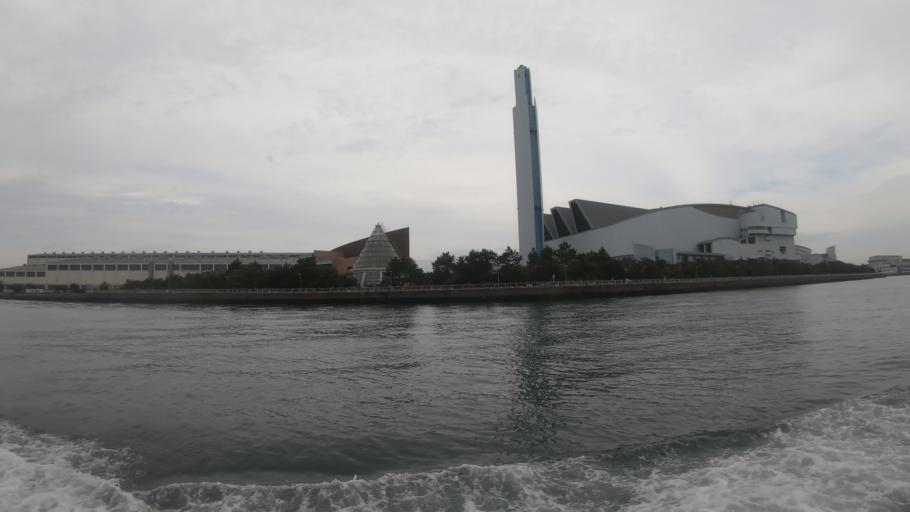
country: JP
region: Kanagawa
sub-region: Kawasaki-shi
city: Kawasaki
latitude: 35.4780
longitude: 139.6898
